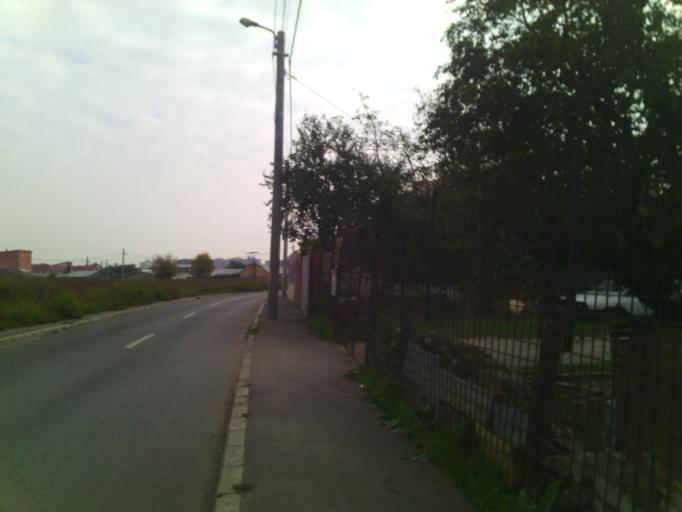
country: RO
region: Bucuresti
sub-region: Municipiul Bucuresti
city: Bucuresti
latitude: 44.3881
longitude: 26.0715
